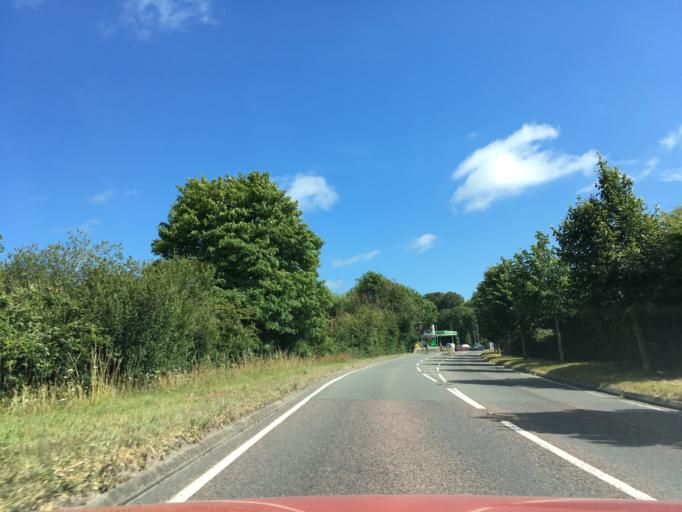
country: GB
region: England
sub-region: Dorset
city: Dorchester
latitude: 50.7200
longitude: -2.4436
